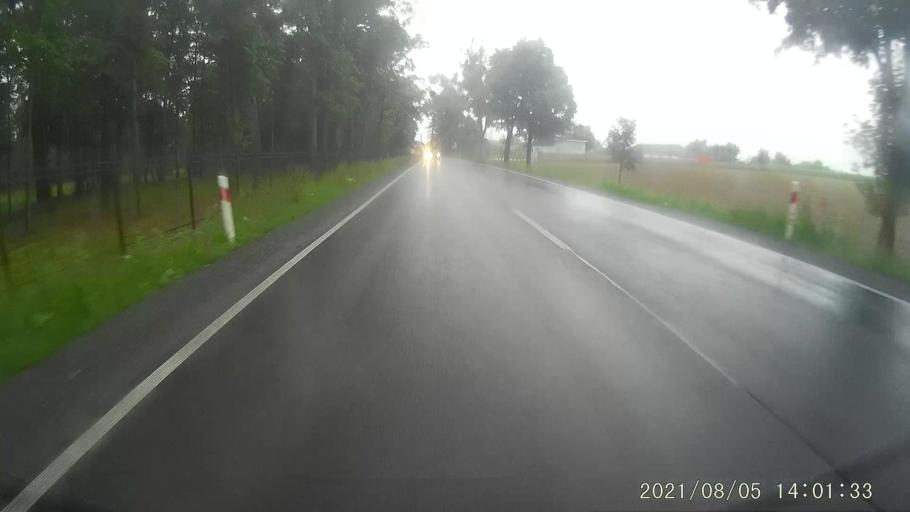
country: PL
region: Opole Voivodeship
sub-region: Powiat krapkowicki
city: Strzeleczki
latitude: 50.4486
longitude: 17.8906
